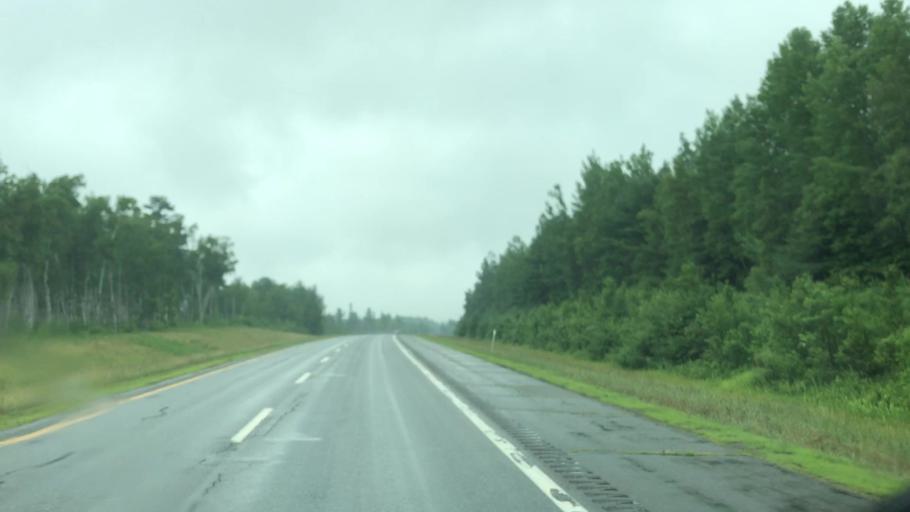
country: US
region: Maine
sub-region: Penobscot County
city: Howland
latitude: 45.1881
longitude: -68.6923
